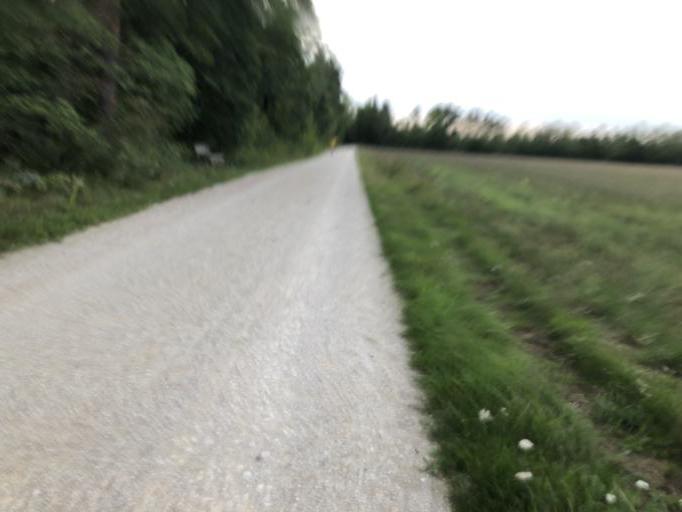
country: DE
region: Bavaria
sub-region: Regierungsbezirk Mittelfranken
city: Uttenreuth
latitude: 49.5879
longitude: 11.0765
